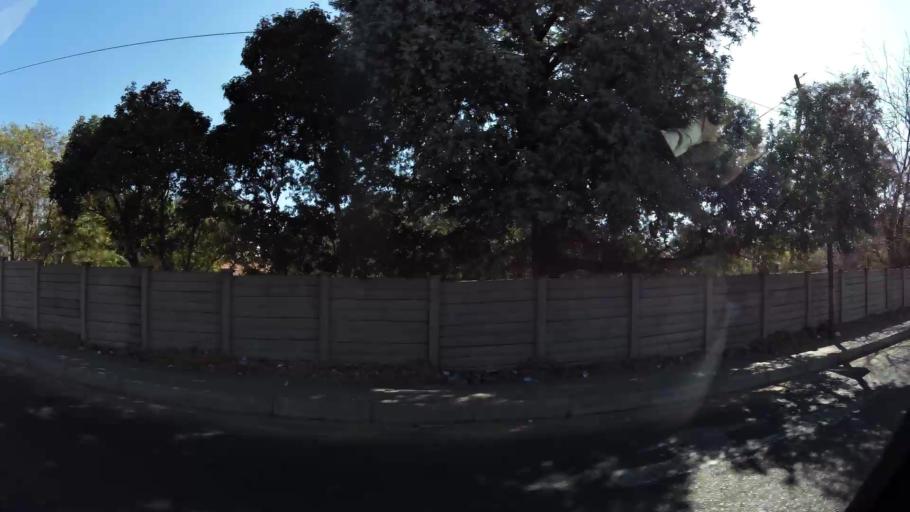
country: ZA
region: Gauteng
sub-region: City of Johannesburg Metropolitan Municipality
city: Roodepoort
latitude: -26.0996
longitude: 27.9405
